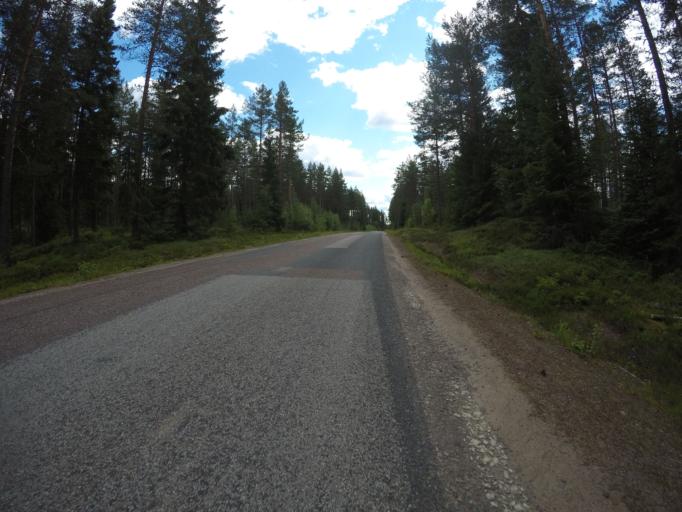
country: SE
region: OErebro
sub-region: Hallefors Kommun
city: Haellefors
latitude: 60.0694
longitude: 14.4932
